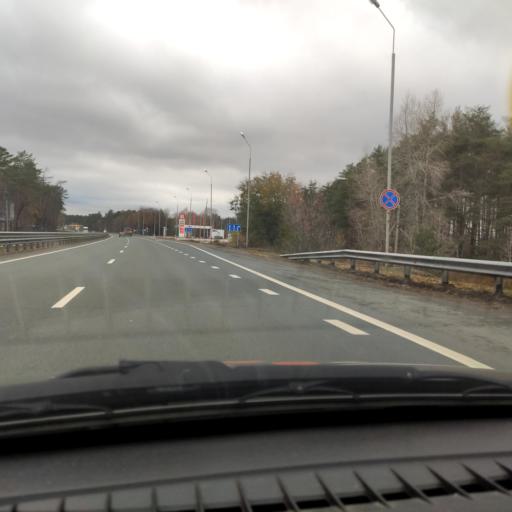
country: RU
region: Samara
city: Zhigulevsk
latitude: 53.5131
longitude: 49.5780
